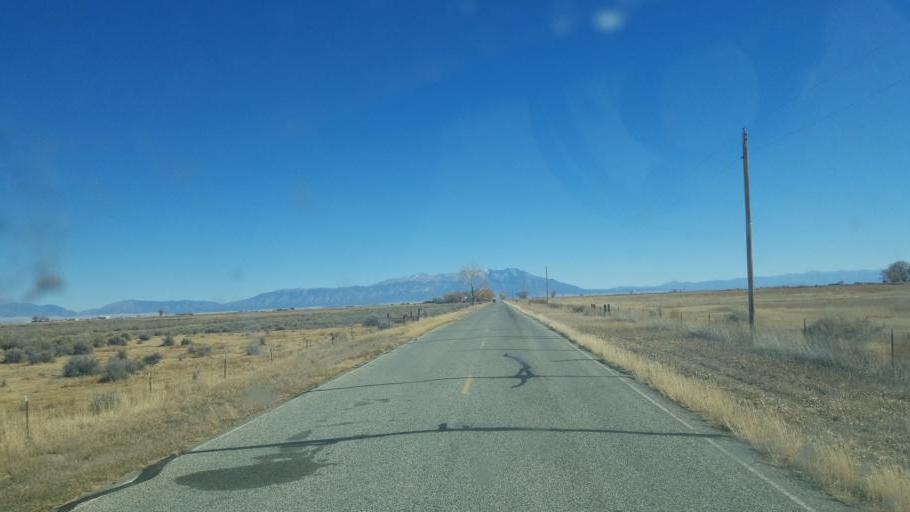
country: US
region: Colorado
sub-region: Alamosa County
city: Alamosa
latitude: 37.5744
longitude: -105.9848
